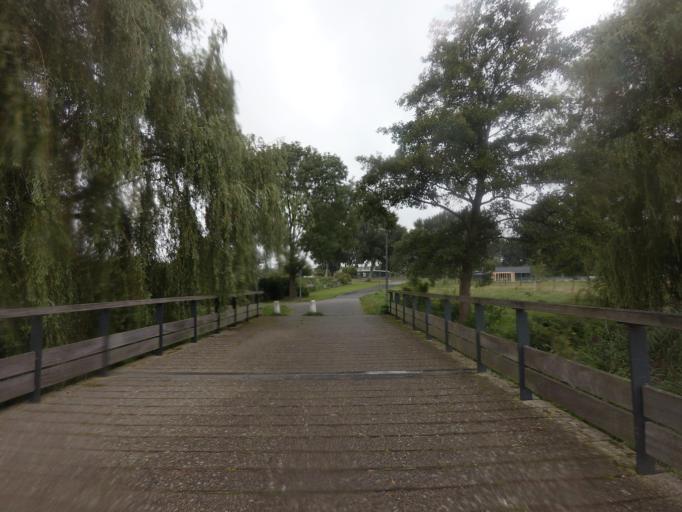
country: NL
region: Flevoland
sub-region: Gemeente Almere
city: Almere Stad
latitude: 52.3488
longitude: 5.2321
